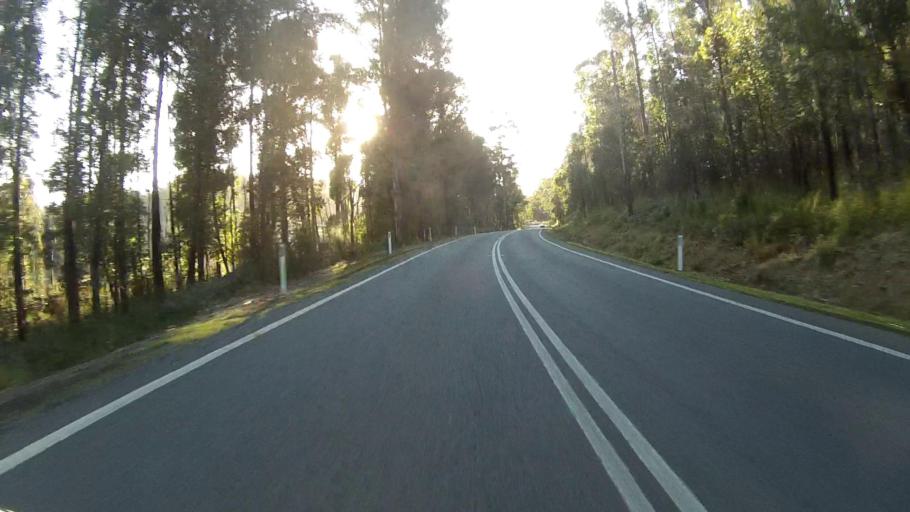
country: AU
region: Tasmania
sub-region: Sorell
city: Sorell
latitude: -42.9827
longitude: 147.9112
